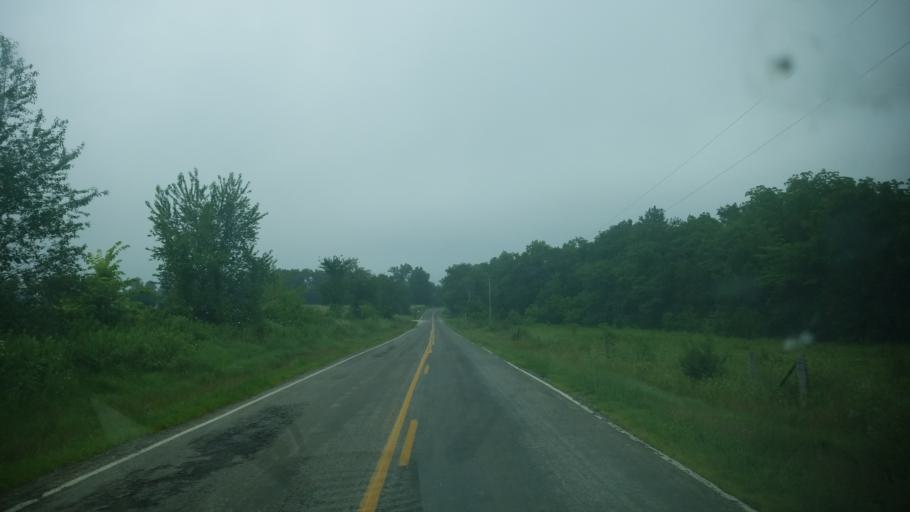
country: US
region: Missouri
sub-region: Audrain County
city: Vandalia
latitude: 39.2955
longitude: -91.3507
